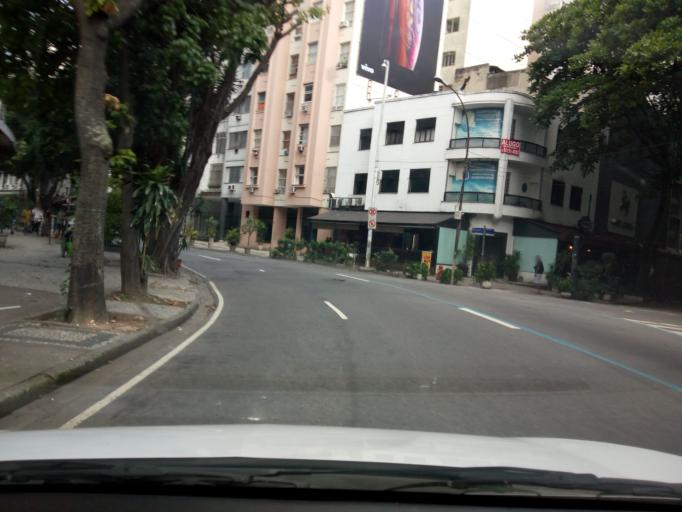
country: BR
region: Rio de Janeiro
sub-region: Rio De Janeiro
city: Rio de Janeiro
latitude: -22.9847
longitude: -43.1955
